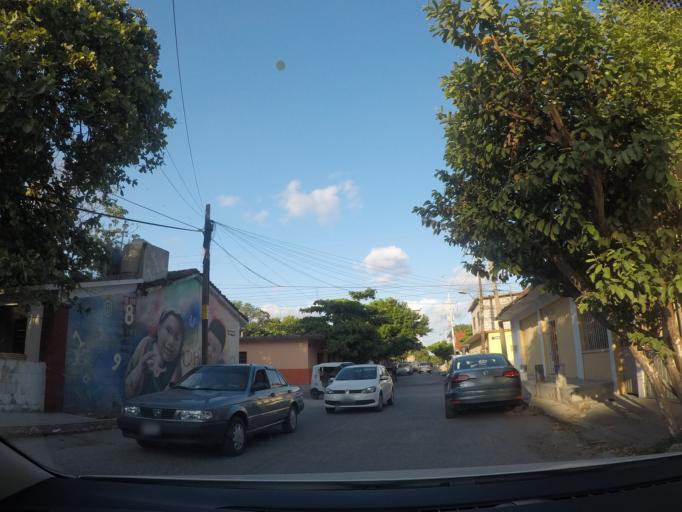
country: MX
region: Oaxaca
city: Juchitan de Zaragoza
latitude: 16.4424
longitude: -95.0245
